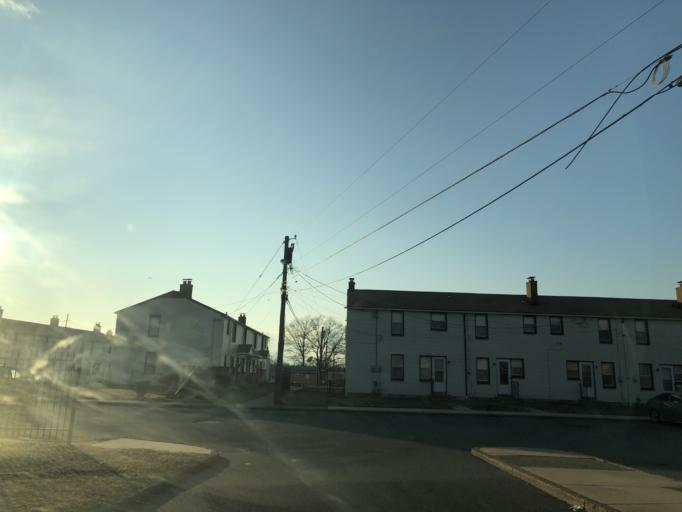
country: US
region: New Jersey
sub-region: Camden County
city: Camden
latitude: 39.9241
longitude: -75.1092
